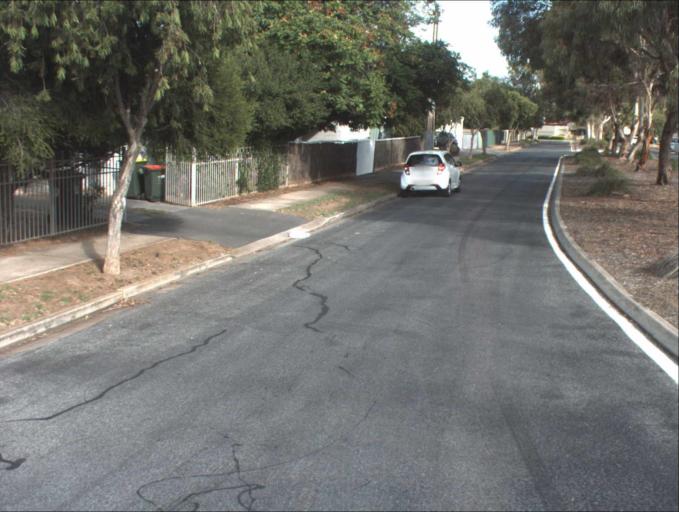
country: AU
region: South Australia
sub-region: Port Adelaide Enfield
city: Klemzig
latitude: -34.8770
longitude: 138.6193
